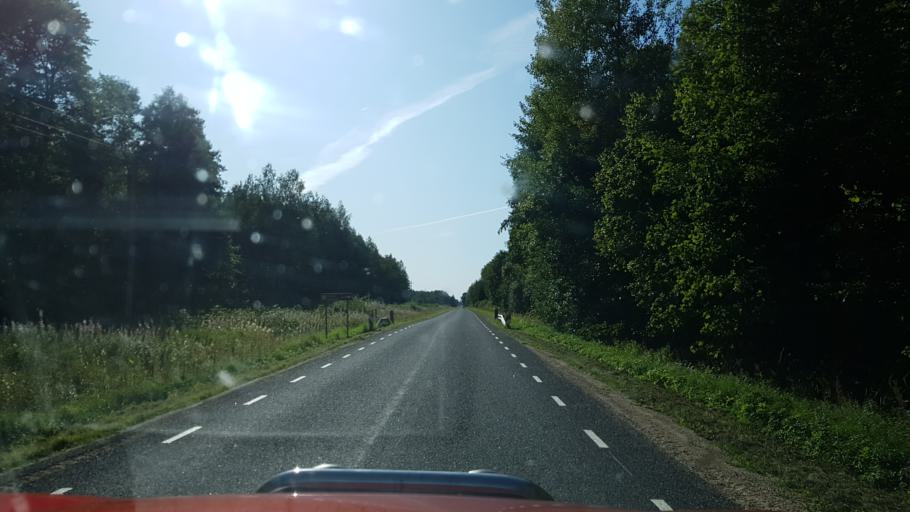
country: LV
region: Aloja
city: Staicele
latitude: 58.0907
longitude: 24.6513
